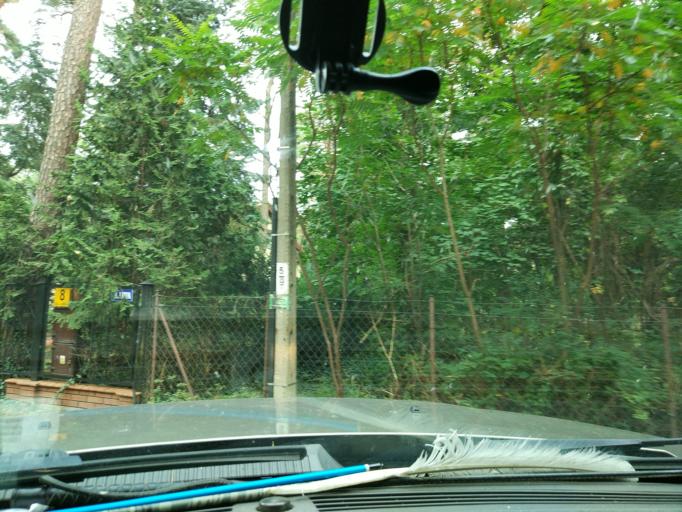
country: PL
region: Masovian Voivodeship
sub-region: Powiat grodziski
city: Podkowa Lesna
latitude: 52.1254
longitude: 20.7392
